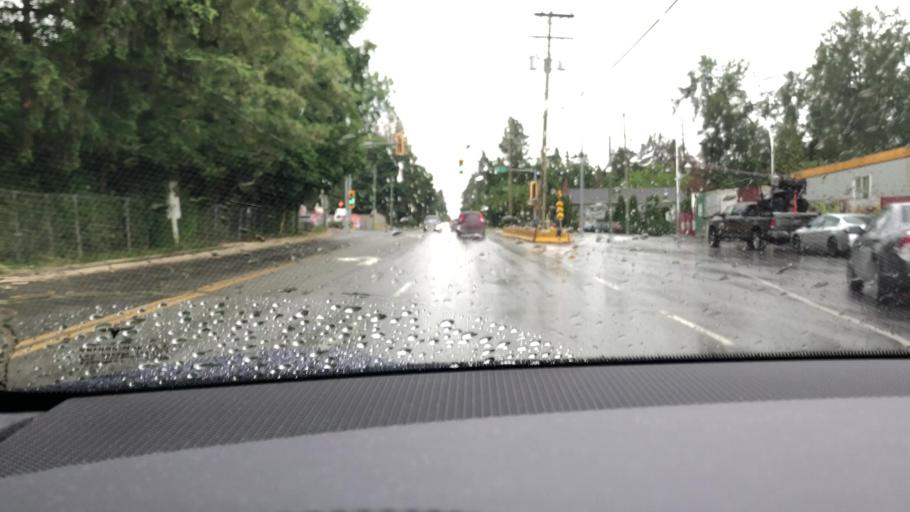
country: CA
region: British Columbia
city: Walnut Grove
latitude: 49.1327
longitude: -122.6459
